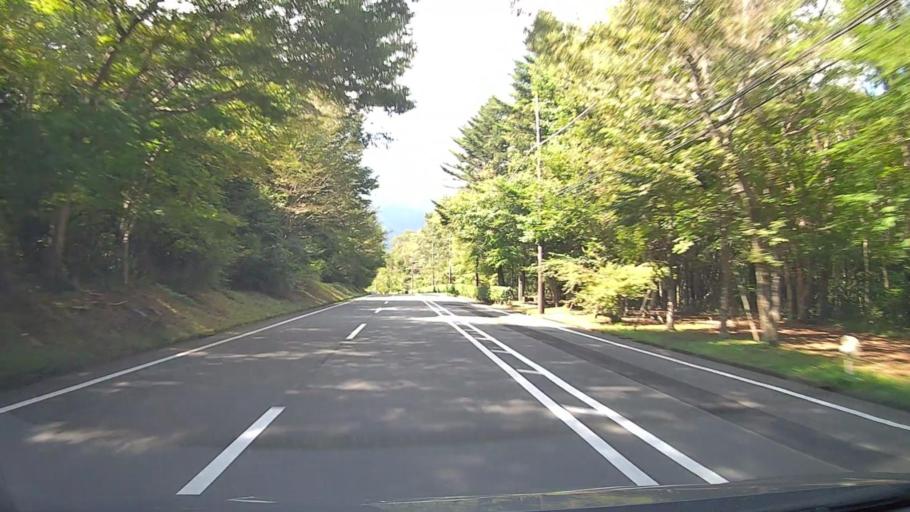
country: JP
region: Shizuoka
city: Gotemba
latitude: 35.3620
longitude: 138.9167
